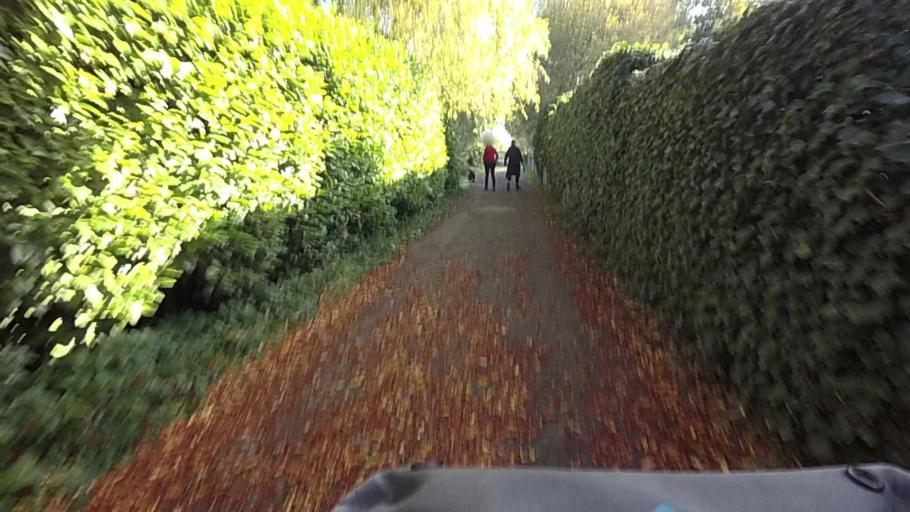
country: NL
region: Utrecht
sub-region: Stichtse Vecht
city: Vreeland
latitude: 52.2251
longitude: 5.0341
